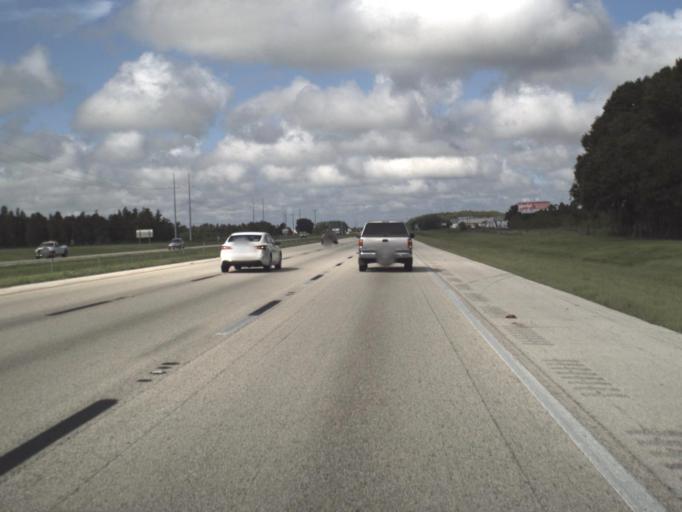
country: US
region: Florida
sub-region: Polk County
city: Polk City
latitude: 28.1456
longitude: -81.8796
